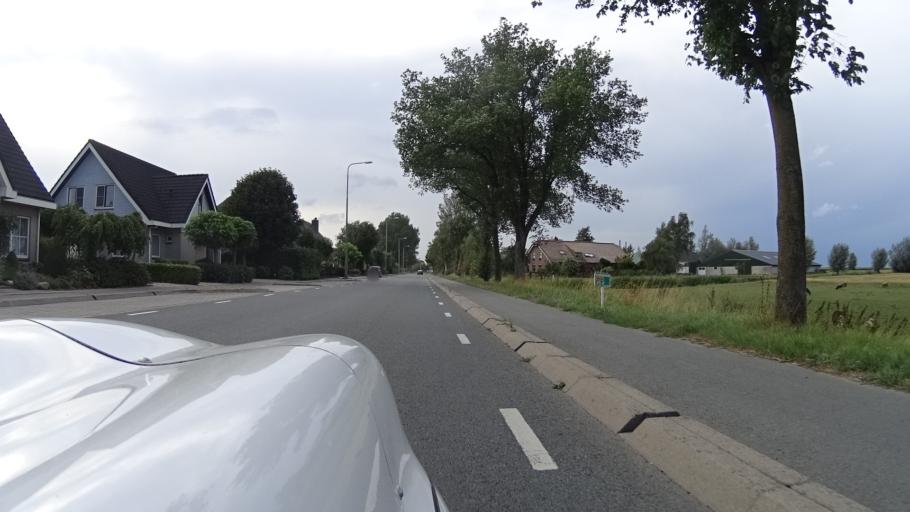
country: NL
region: South Holland
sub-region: Bodegraven-Reeuwijk
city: Bodegraven
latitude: 52.0804
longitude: 4.8077
